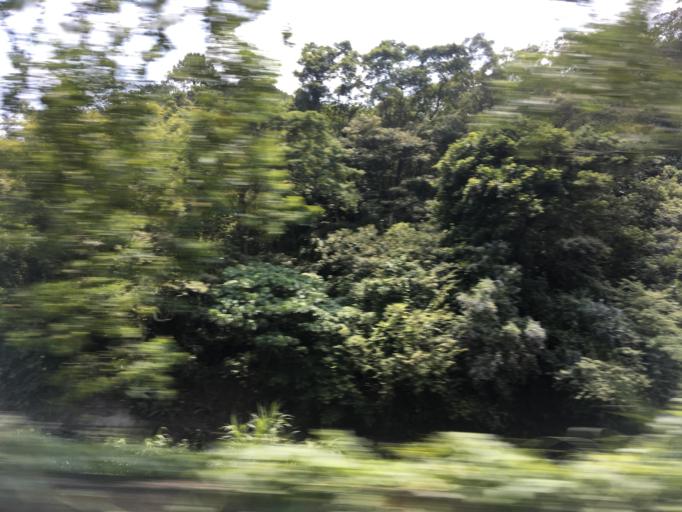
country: TW
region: Taiwan
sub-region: Yilan
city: Yilan
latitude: 24.8140
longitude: 121.7420
